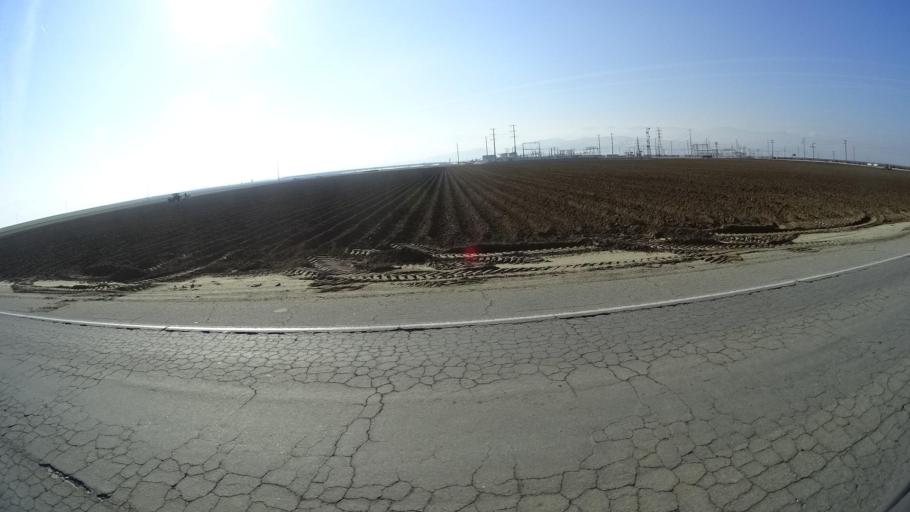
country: US
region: California
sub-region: Kern County
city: Weedpatch
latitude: 35.0935
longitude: -118.9735
